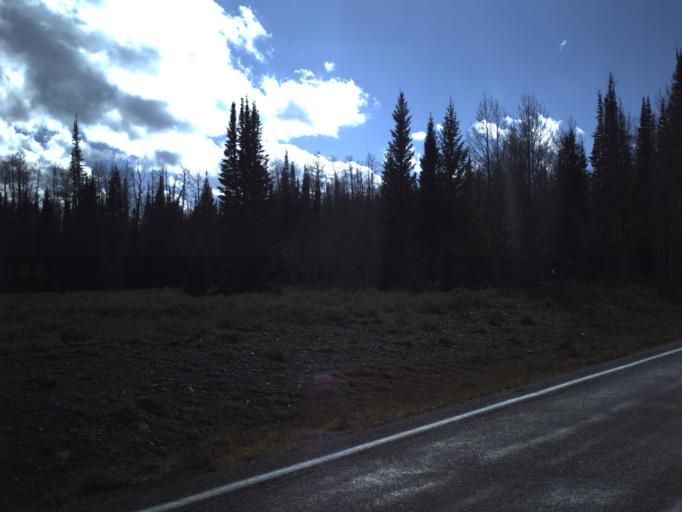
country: US
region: Utah
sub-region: Iron County
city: Parowan
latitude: 37.6549
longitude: -112.7630
